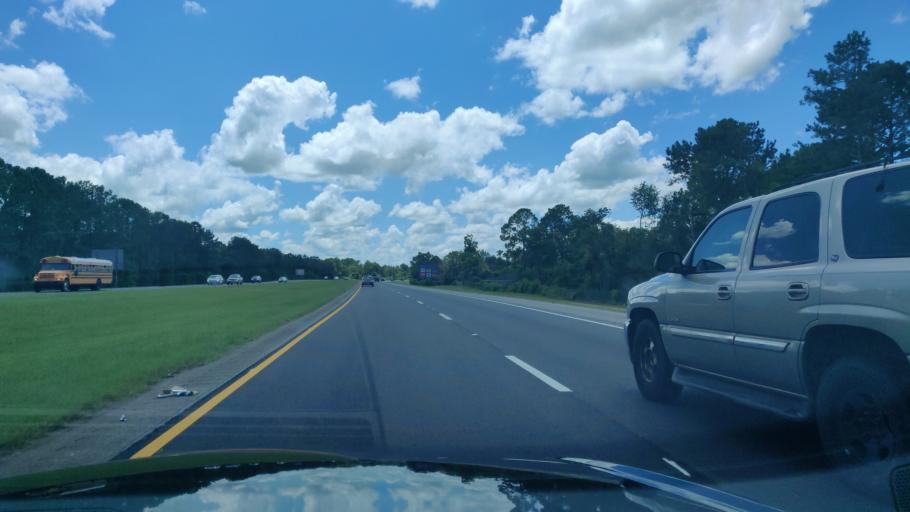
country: US
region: Georgia
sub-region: Dougherty County
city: Albany
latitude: 31.6162
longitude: -84.1885
